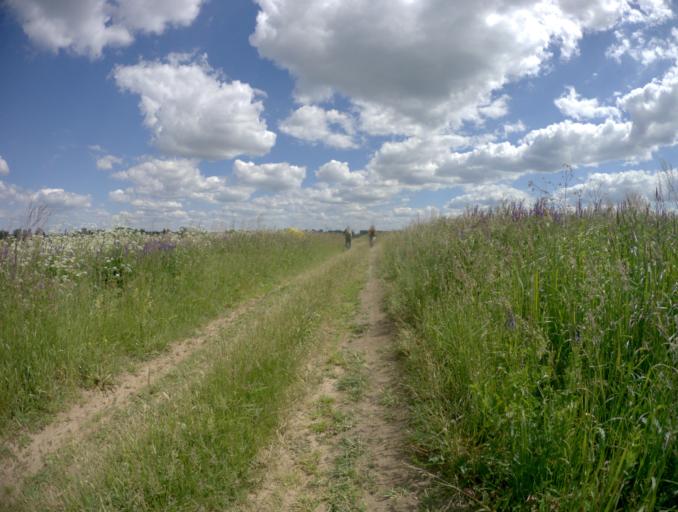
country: RU
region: Vladimir
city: Bogolyubovo
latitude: 56.1839
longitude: 40.4949
